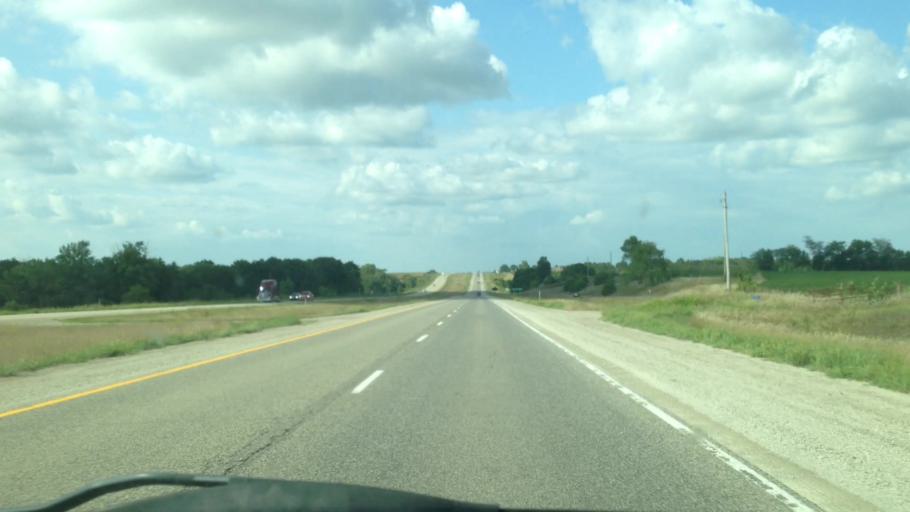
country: US
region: Iowa
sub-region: Henry County
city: Mount Pleasant
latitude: 40.8319
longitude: -91.5644
